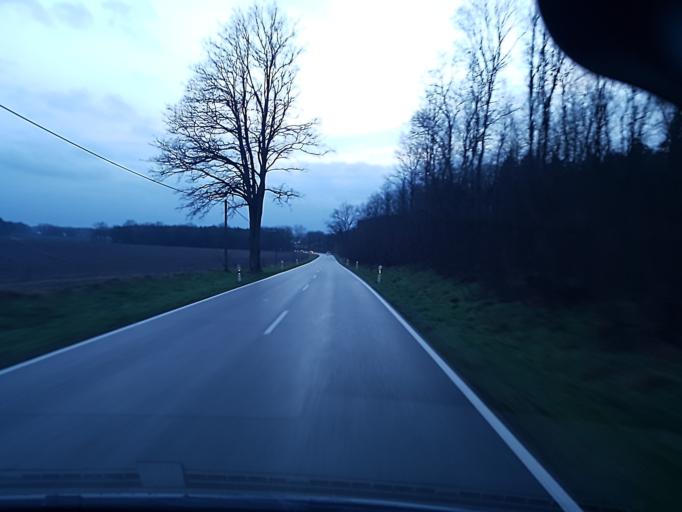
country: DE
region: Brandenburg
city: Bronkow
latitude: 51.6614
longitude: 13.9050
